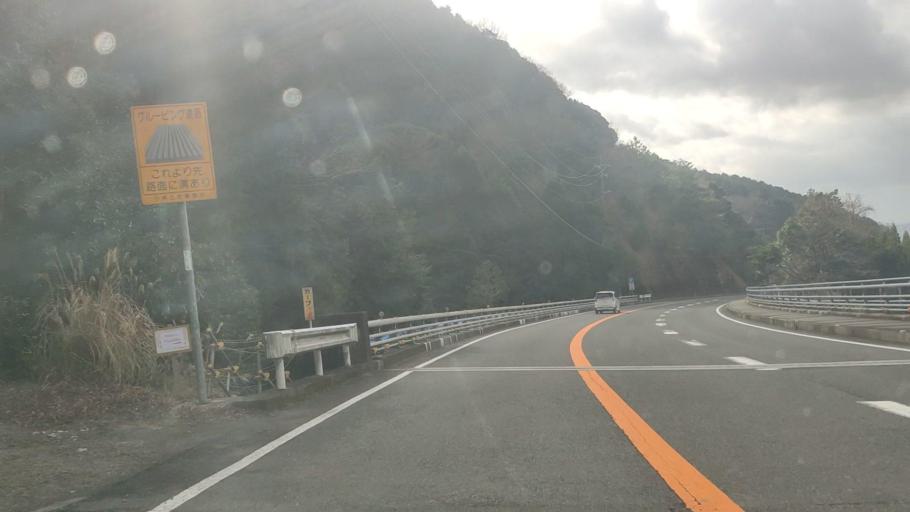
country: JP
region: Kumamoto
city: Hitoyoshi
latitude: 32.0774
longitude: 130.8030
